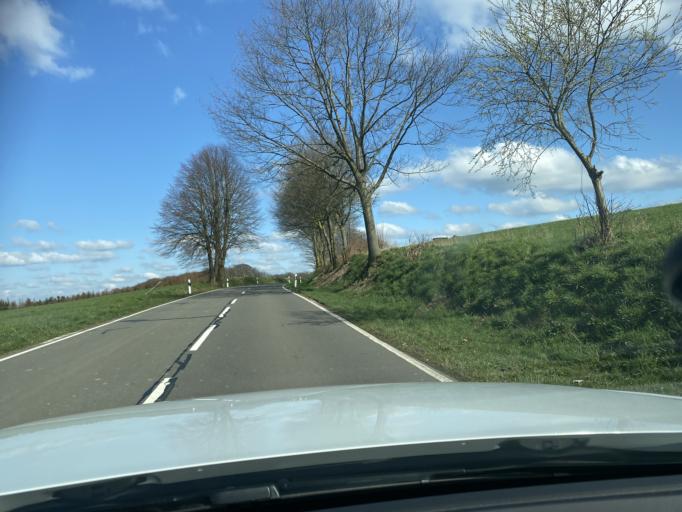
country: DE
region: North Rhine-Westphalia
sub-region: Regierungsbezirk Koln
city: Lindlar
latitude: 51.0066
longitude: 7.3316
